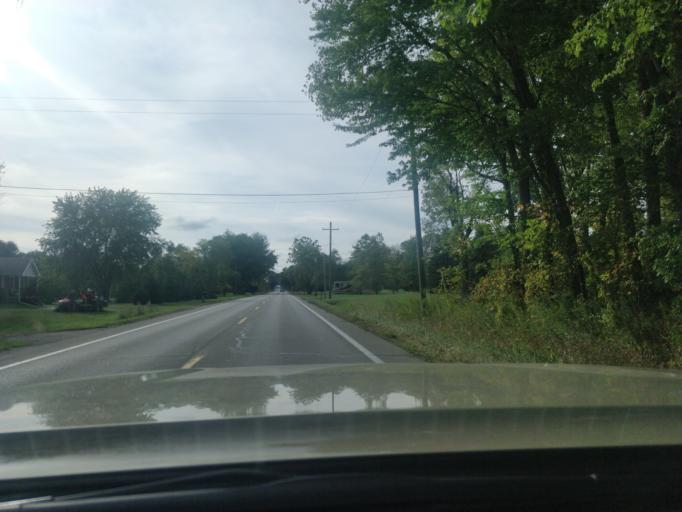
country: US
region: Michigan
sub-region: Wayne County
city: Romulus
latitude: 42.1662
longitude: -83.3491
